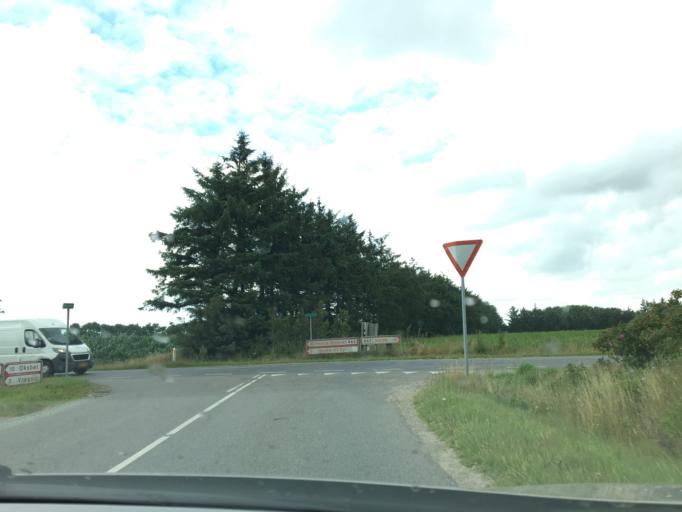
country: DK
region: South Denmark
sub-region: Varde Kommune
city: Oksbol
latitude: 55.7003
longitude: 8.3205
